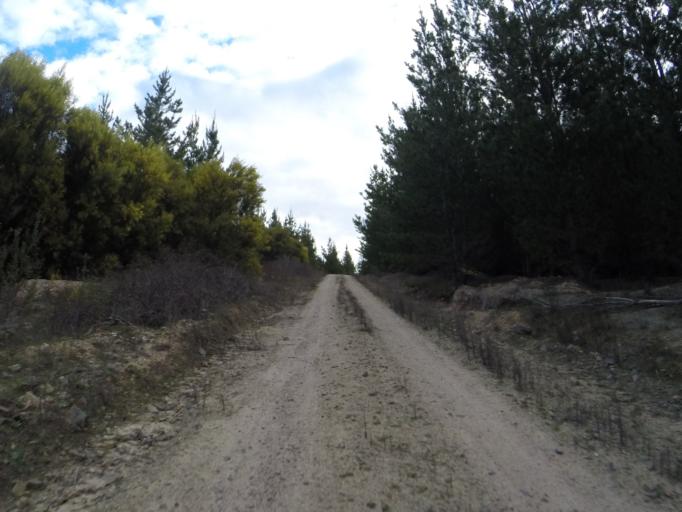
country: AU
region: Australian Capital Territory
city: Macquarie
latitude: -35.3473
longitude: 148.9492
